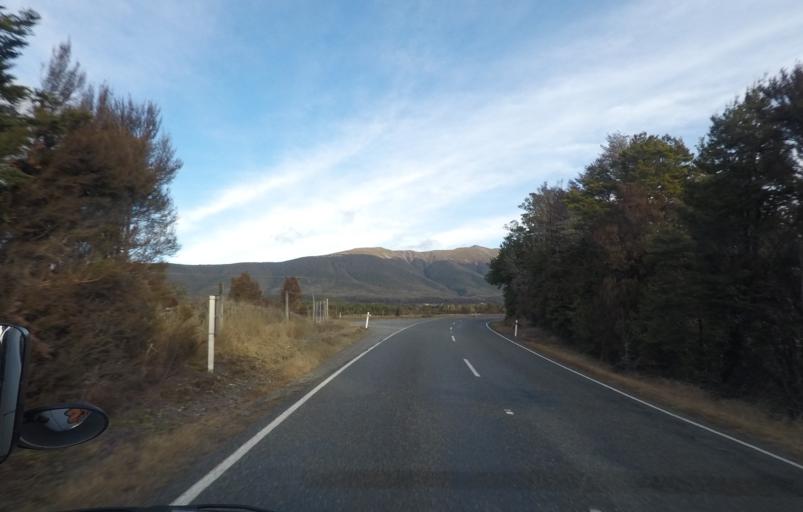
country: NZ
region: Tasman
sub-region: Tasman District
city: Wakefield
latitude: -41.7657
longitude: 172.8942
